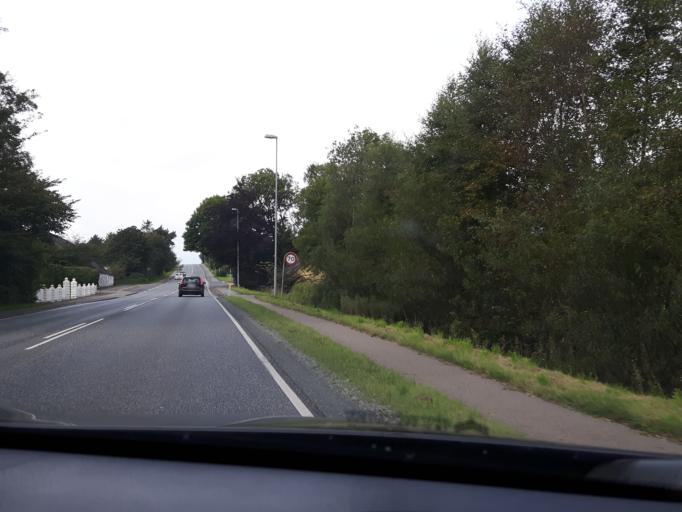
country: DK
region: North Denmark
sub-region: Jammerbugt Kommune
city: Brovst
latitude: 57.0951
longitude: 9.4791
